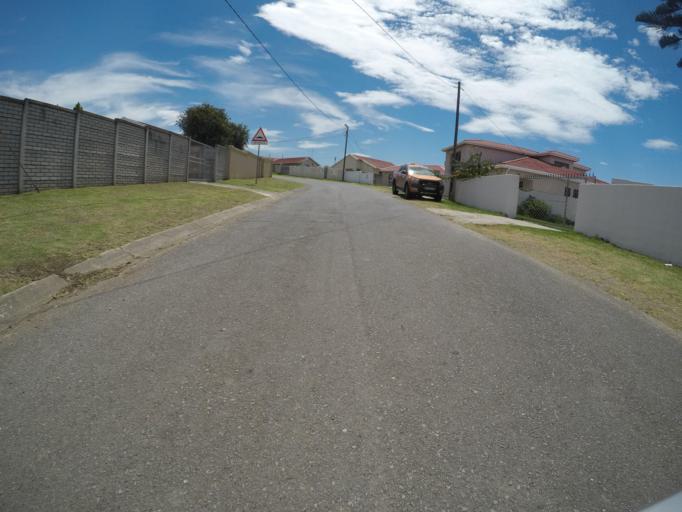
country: ZA
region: Eastern Cape
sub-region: Buffalo City Metropolitan Municipality
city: East London
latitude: -33.0425
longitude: 27.8644
